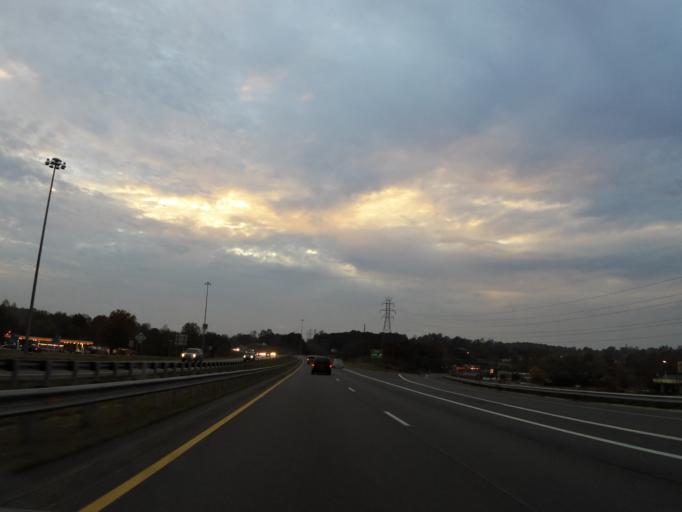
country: US
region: North Carolina
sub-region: Burke County
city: Morganton
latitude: 35.7233
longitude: -81.6531
